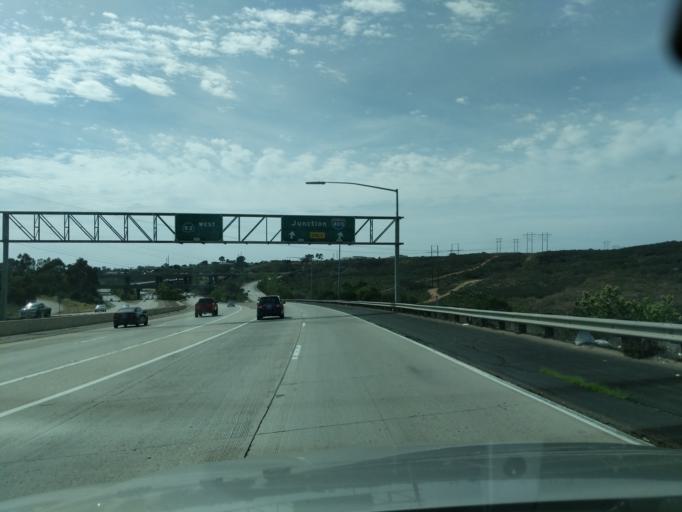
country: US
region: California
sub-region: San Diego County
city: La Jolla
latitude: 32.8470
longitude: -117.1700
